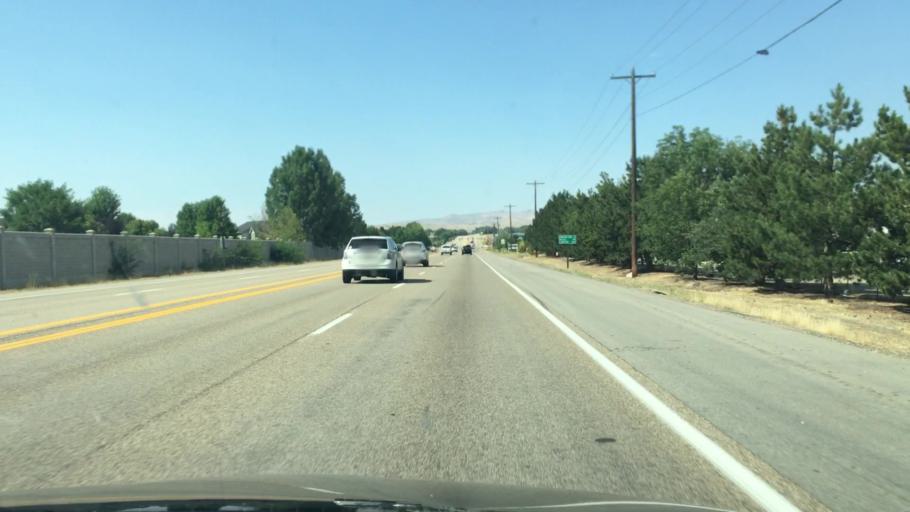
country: US
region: Idaho
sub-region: Ada County
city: Eagle
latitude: 43.6879
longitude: -116.3192
